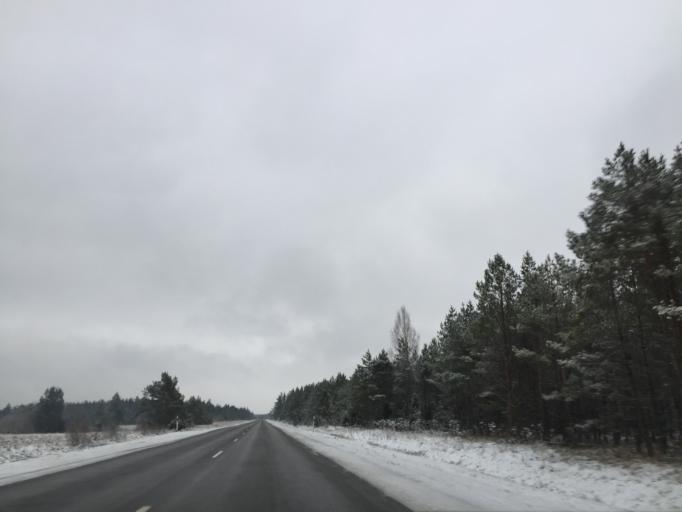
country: EE
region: Laeaene
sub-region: Lihula vald
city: Lihula
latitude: 58.6206
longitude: 23.9043
